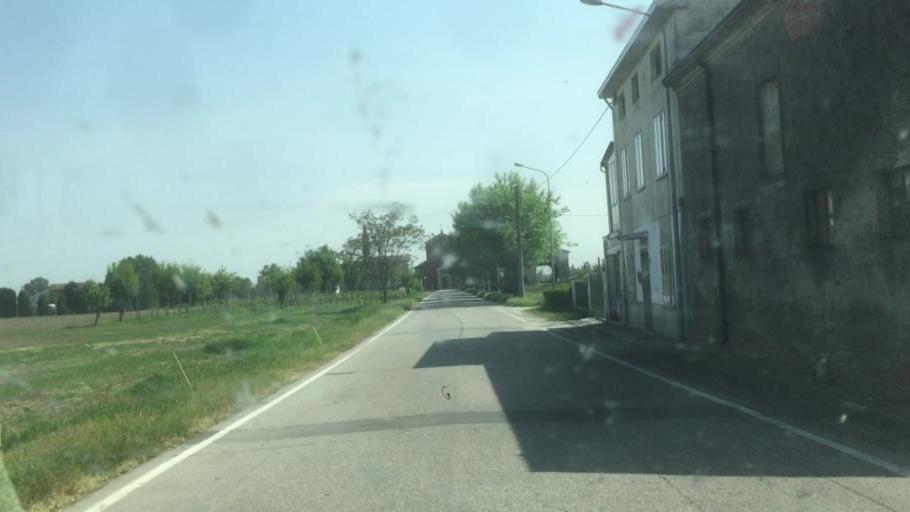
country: IT
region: Lombardy
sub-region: Provincia di Mantova
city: Commessaggio
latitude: 44.9996
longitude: 10.5864
